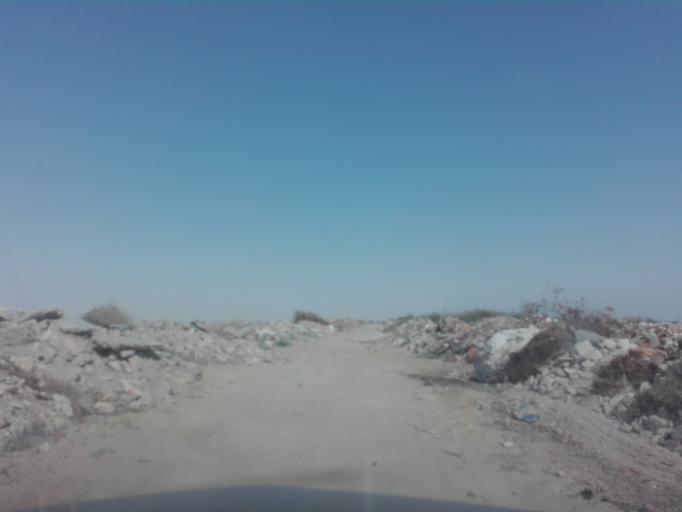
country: TN
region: Qabis
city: Gabes
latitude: 33.9600
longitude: 10.0672
